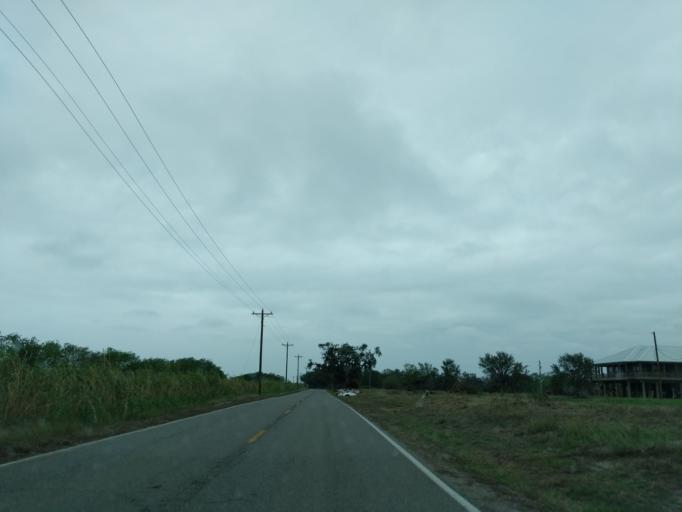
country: US
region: Louisiana
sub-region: Jefferson Davis Parish
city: Lake Arthur
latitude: 29.7517
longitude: -92.9074
